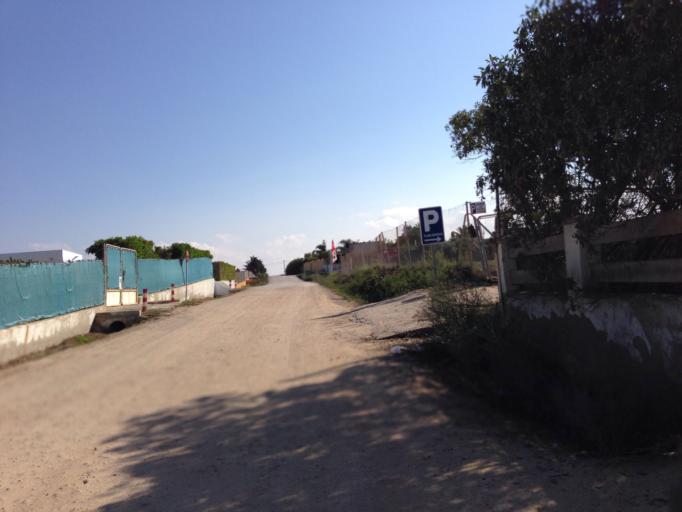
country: ES
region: Andalusia
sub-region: Provincia de Cadiz
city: Conil de la Frontera
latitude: 36.2179
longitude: -6.0597
